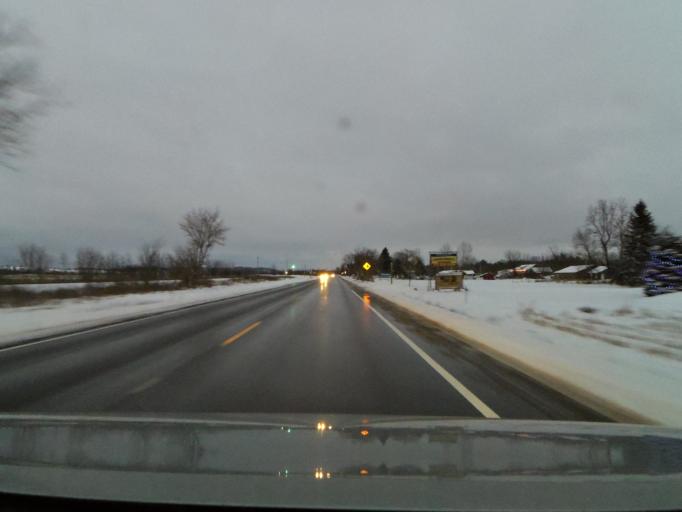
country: US
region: Wisconsin
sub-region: Dunn County
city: Boyceville
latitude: 44.9387
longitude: -92.0180
